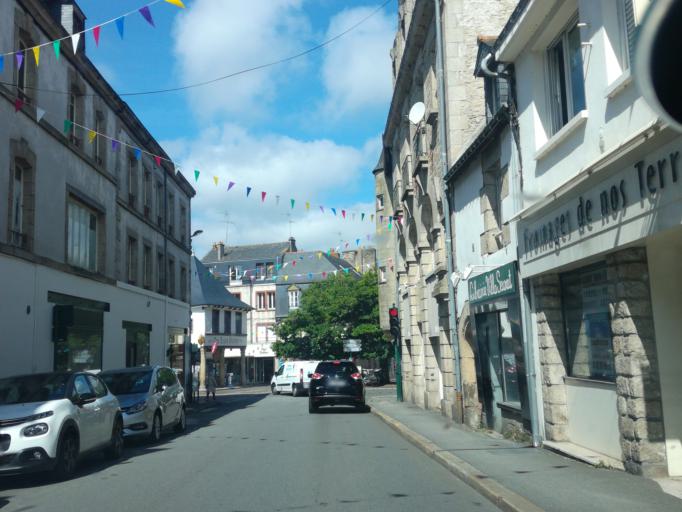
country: FR
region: Brittany
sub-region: Departement du Morbihan
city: Pontivy
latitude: 48.0680
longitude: -2.9645
